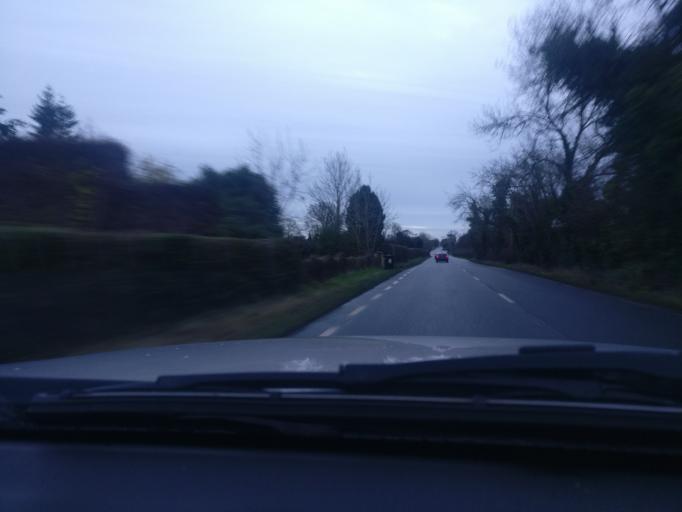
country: IE
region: Leinster
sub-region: An Mhi
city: Navan
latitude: 53.6893
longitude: -6.7743
